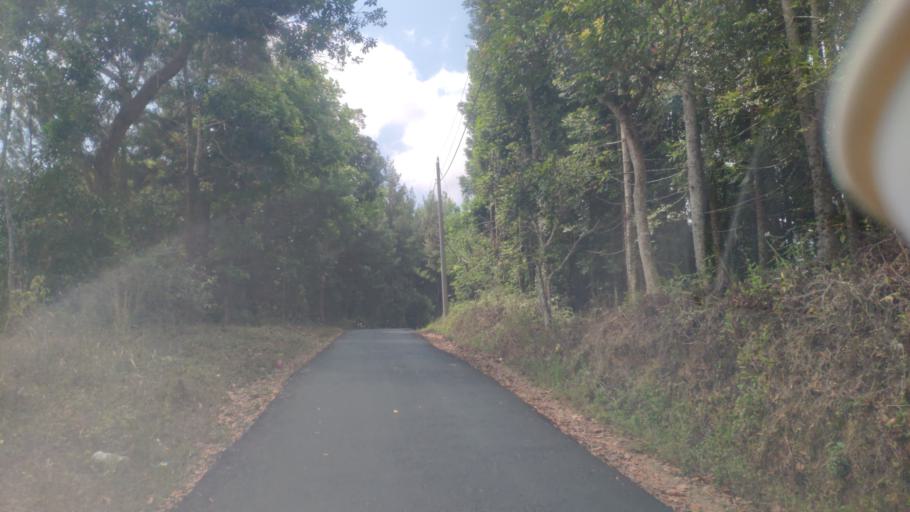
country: ID
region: Central Java
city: Wonosobo
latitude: -7.4504
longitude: 109.7153
